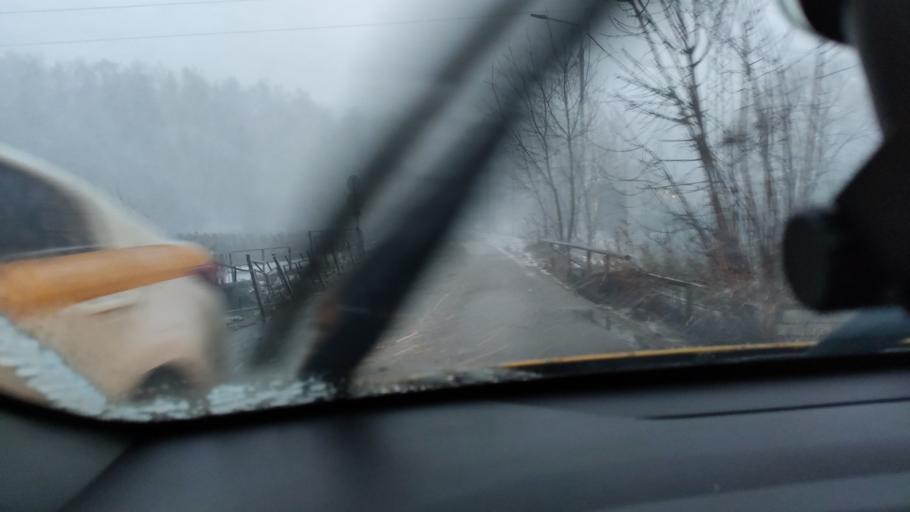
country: RU
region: Moskovskaya
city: Biryulevo Zapadnoye
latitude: 55.5594
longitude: 37.6402
